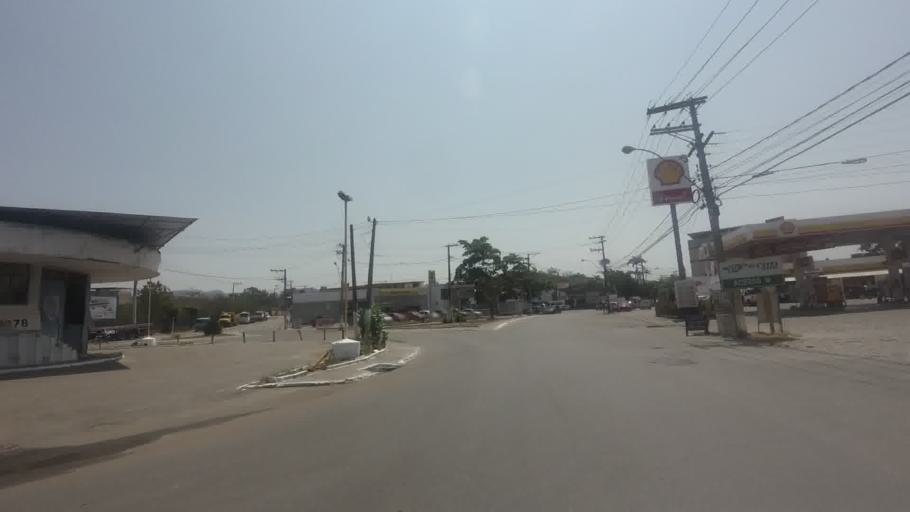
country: BR
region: Espirito Santo
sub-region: Cachoeiro De Itapemirim
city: Cachoeiro de Itapemirim
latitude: -20.8417
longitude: -41.1585
